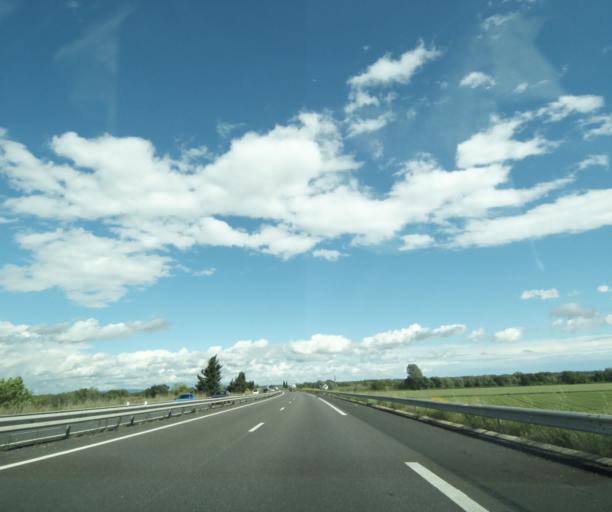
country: FR
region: Languedoc-Roussillon
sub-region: Departement du Gard
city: Bellegarde
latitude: 43.7330
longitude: 4.4704
